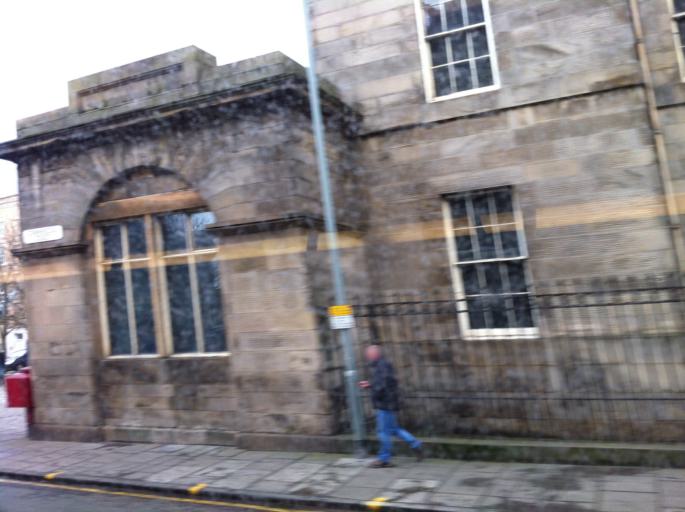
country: GB
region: Scotland
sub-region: West Lothian
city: Seafield
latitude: 55.9763
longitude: -3.1701
